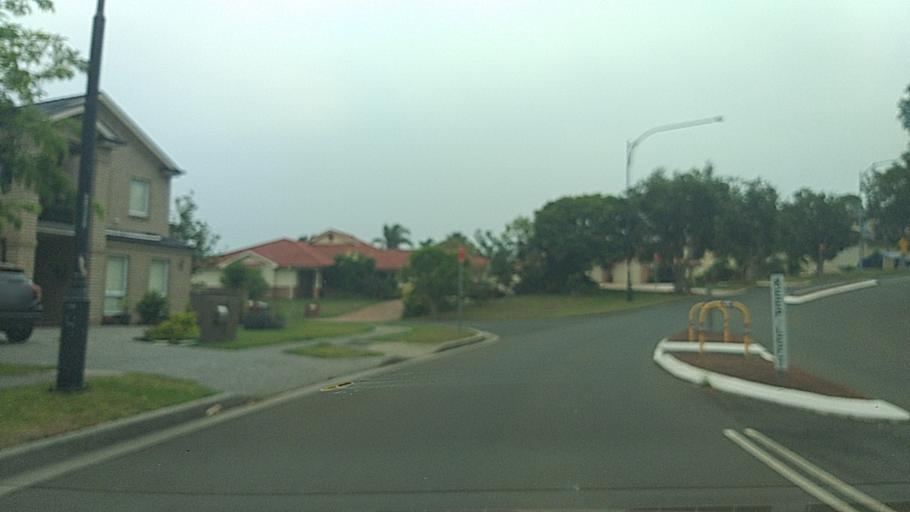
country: AU
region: New South Wales
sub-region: Shellharbour
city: Flinders
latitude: -34.5831
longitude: 150.8475
